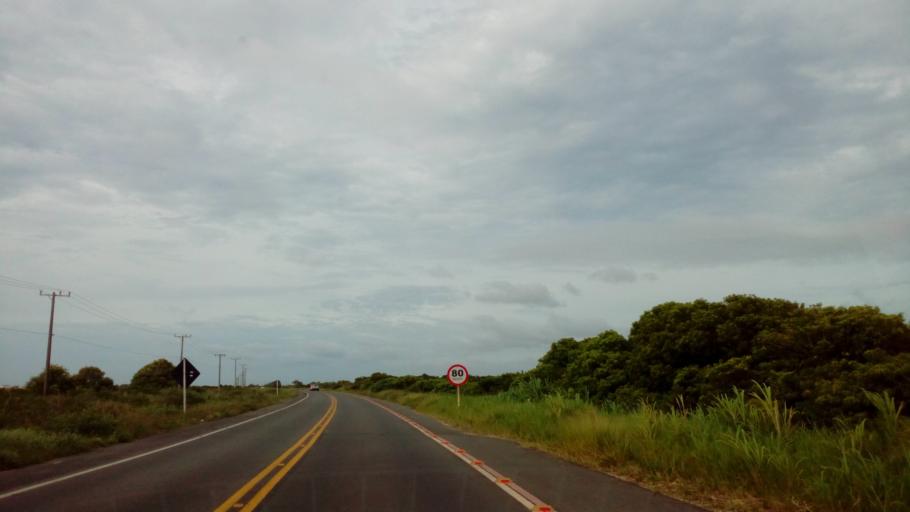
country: BR
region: Santa Catarina
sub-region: Laguna
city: Laguna
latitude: -28.5772
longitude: -48.8230
